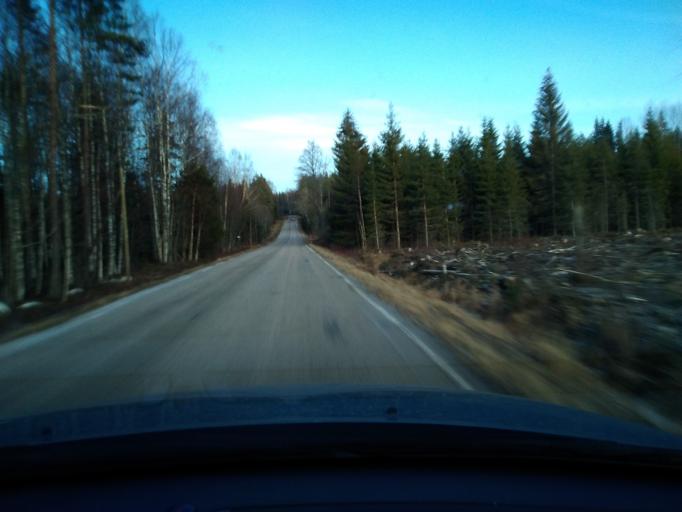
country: FI
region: Haeme
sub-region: Haemeenlinna
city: Renko
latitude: 60.7529
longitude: 24.1999
